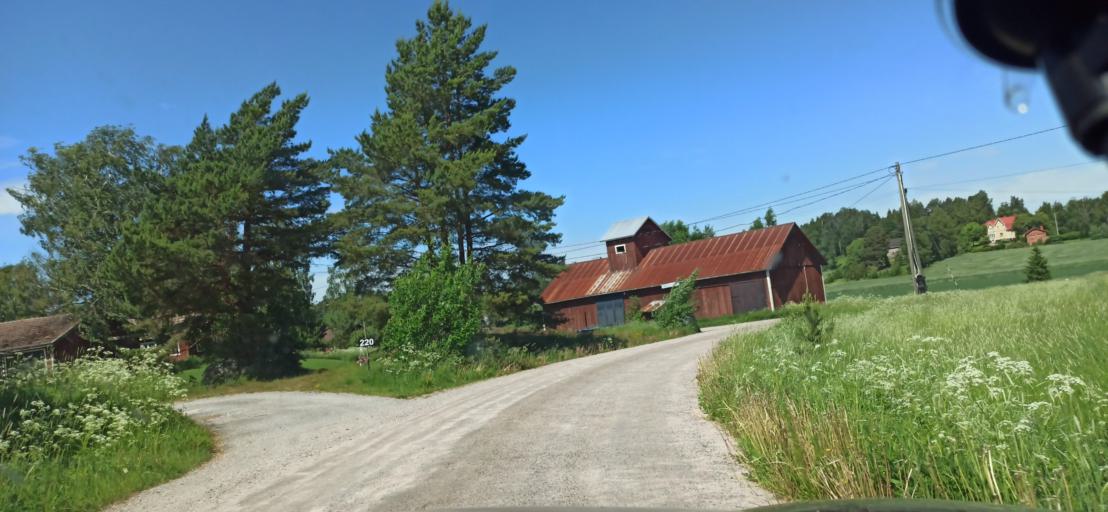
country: FI
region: Varsinais-Suomi
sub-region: Turku
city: Sauvo
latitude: 60.3840
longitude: 22.6337
